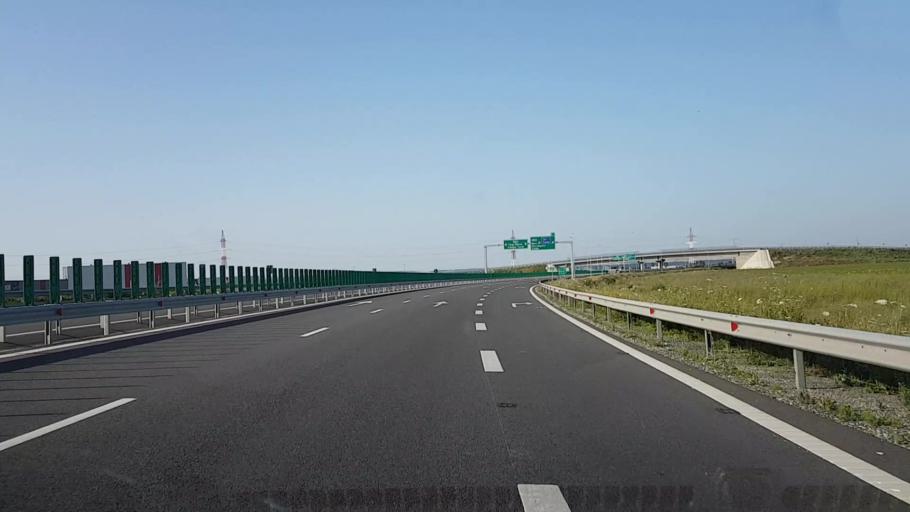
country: RO
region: Cluj
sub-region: Comuna Mihai Viteazu
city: Mihai Viteazu
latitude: 46.5148
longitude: 23.7837
